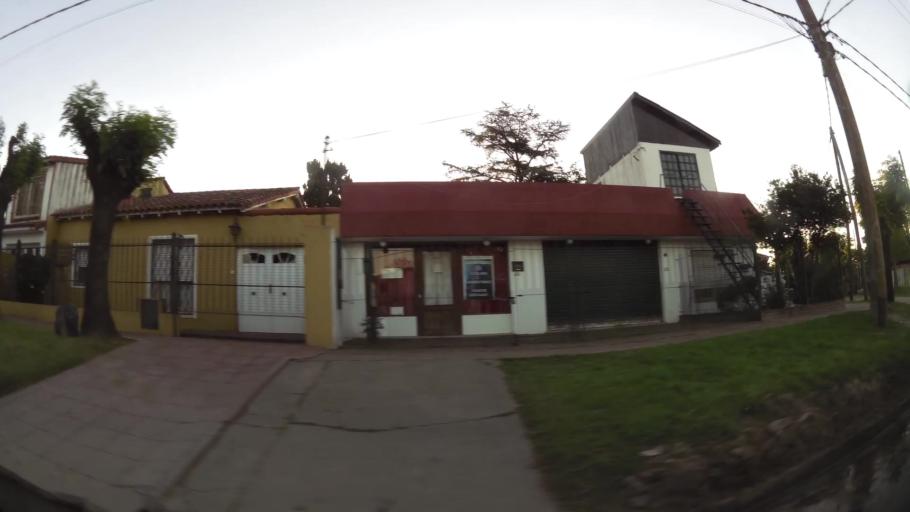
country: AR
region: Buenos Aires
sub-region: Partido de Almirante Brown
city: Adrogue
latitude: -34.7986
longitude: -58.3401
